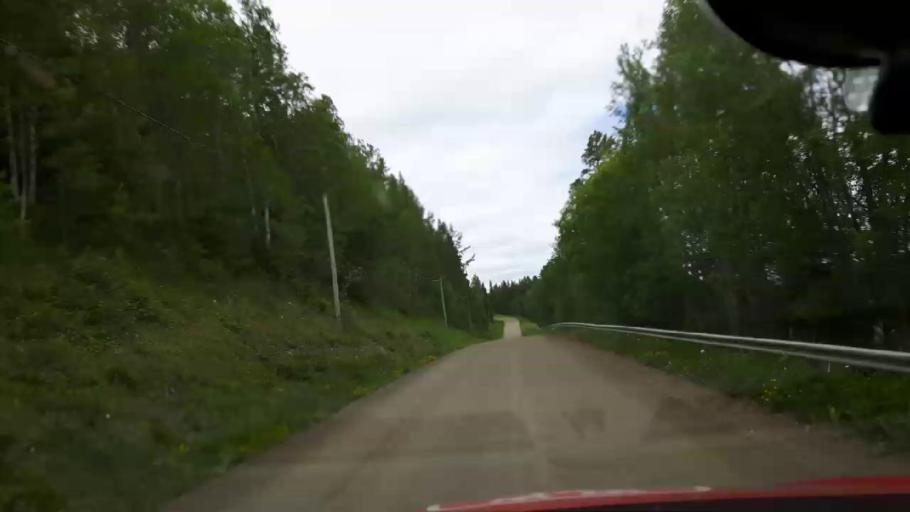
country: SE
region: Jaemtland
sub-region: OEstersunds Kommun
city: Brunflo
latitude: 62.9029
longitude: 15.1109
